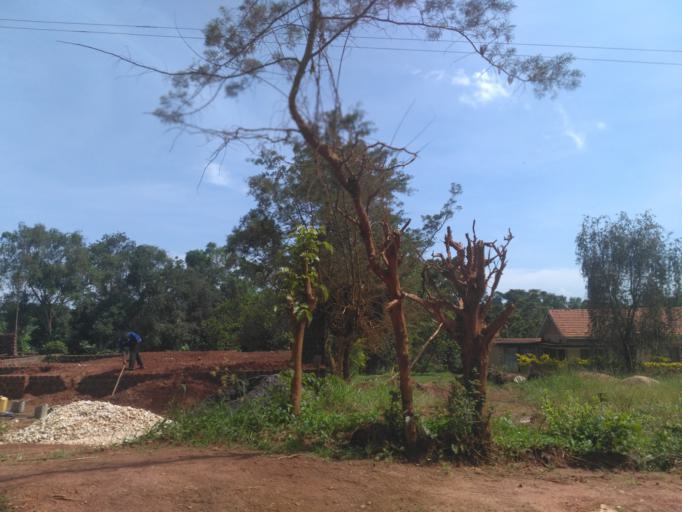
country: UG
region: Central Region
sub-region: Wakiso District
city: Kireka
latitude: 0.4463
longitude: 32.5814
